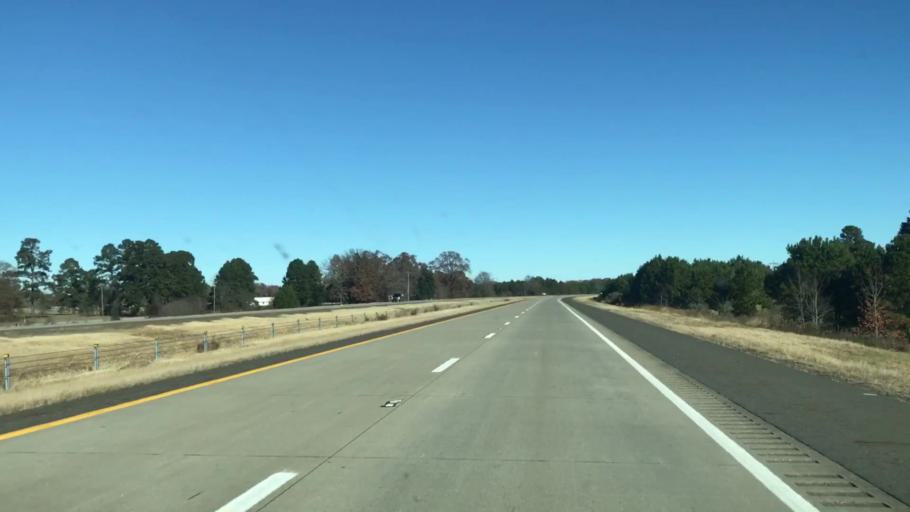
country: US
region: Texas
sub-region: Cass County
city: Queen City
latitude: 33.1961
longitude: -93.8773
